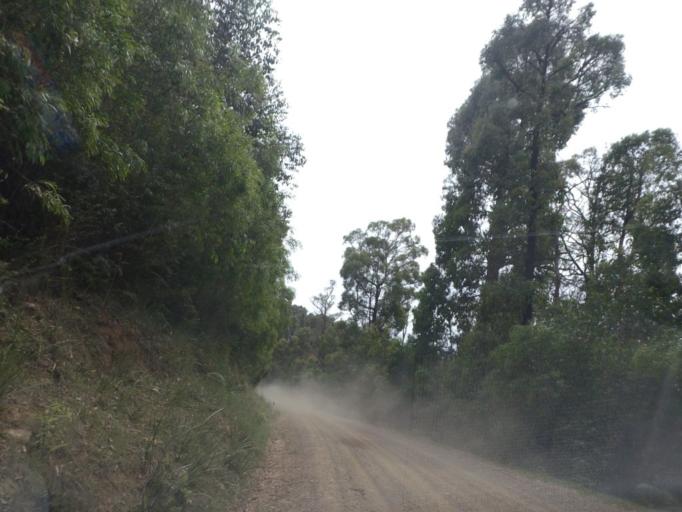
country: AU
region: Victoria
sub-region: Yarra Ranges
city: Healesville
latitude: -37.4539
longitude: 145.5726
